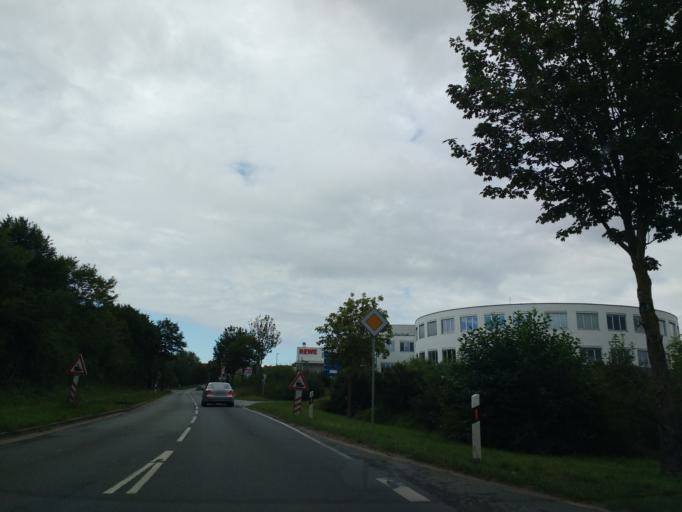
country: DE
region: Lower Saxony
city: Bad Laer
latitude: 52.0971
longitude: 8.0968
